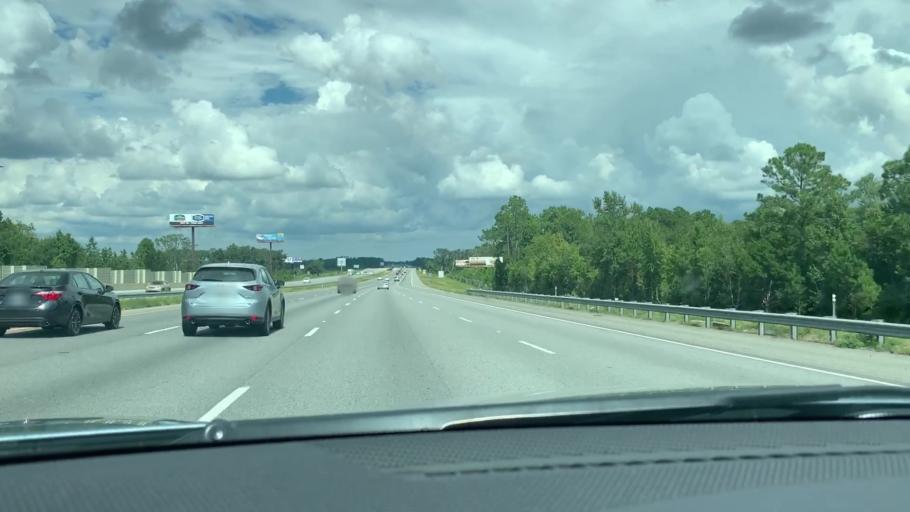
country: US
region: Georgia
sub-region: Glynn County
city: Dock Junction
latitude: 31.1445
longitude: -81.5704
